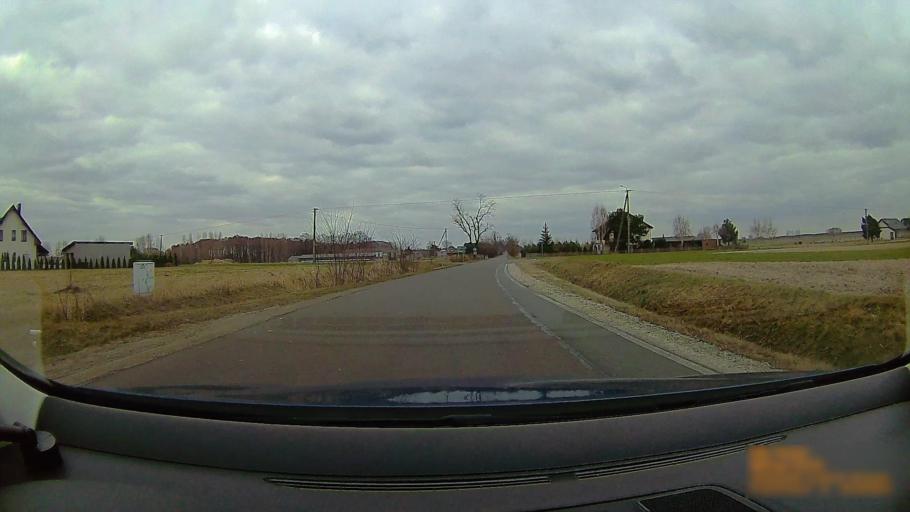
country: PL
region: Greater Poland Voivodeship
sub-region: Powiat koninski
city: Rzgow Pierwszy
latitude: 52.1291
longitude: 18.0499
